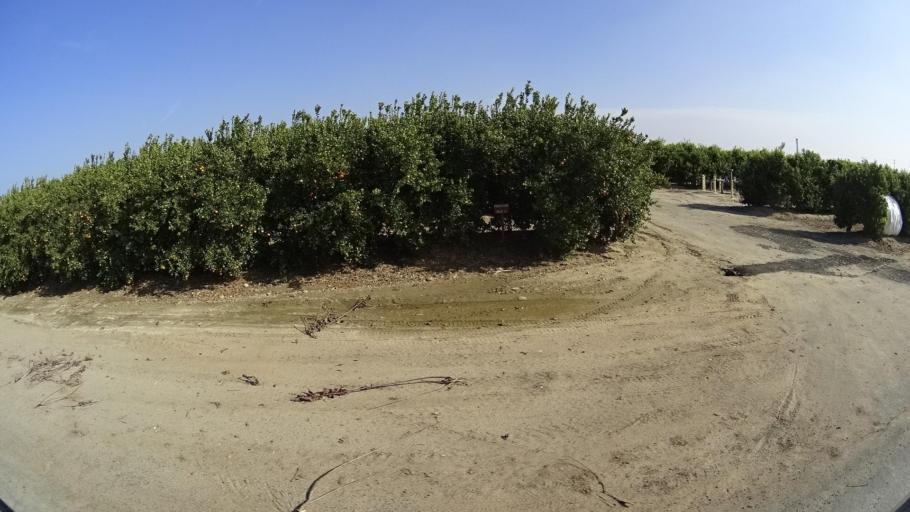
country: US
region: California
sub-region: Kern County
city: McFarland
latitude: 35.6038
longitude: -119.1866
